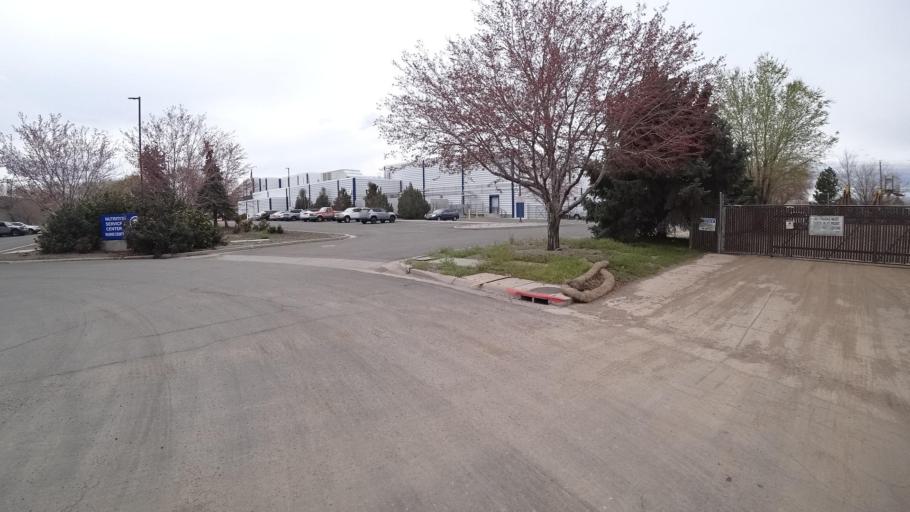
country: US
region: Nevada
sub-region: Washoe County
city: Sparks
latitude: 39.5188
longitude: -119.7390
